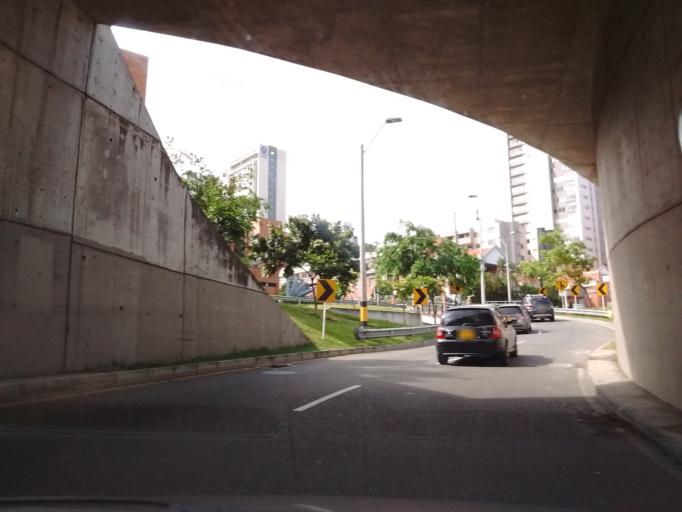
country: CO
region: Antioquia
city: Itagui
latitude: 6.2020
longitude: -75.5754
